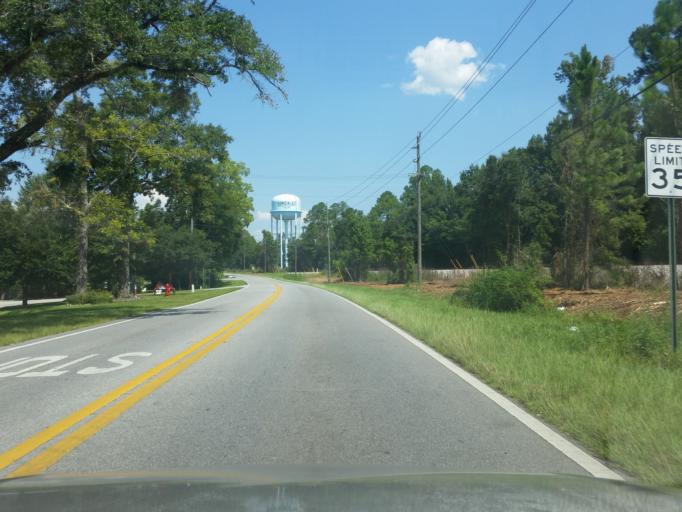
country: US
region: Florida
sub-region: Escambia County
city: Gonzalez
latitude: 30.5807
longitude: -87.2950
